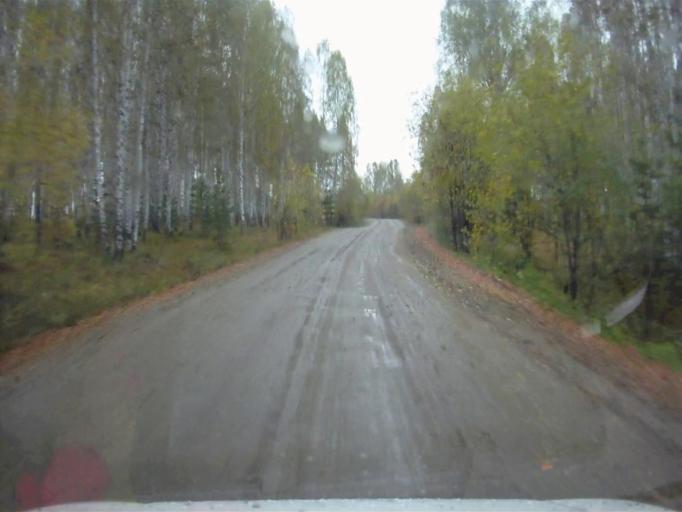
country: RU
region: Chelyabinsk
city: Kyshtym
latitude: 55.8441
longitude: 60.4854
